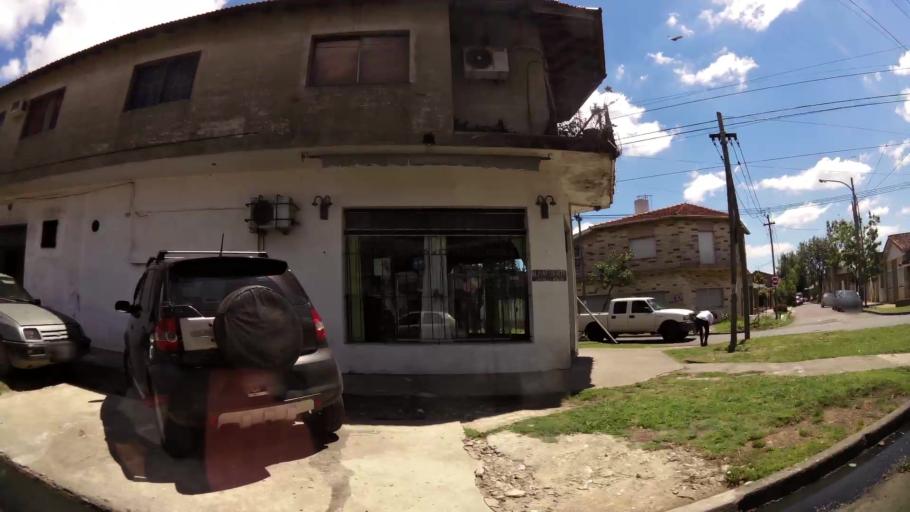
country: AR
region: Buenos Aires
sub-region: Partido de Lanus
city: Lanus
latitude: -34.7291
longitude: -58.4064
